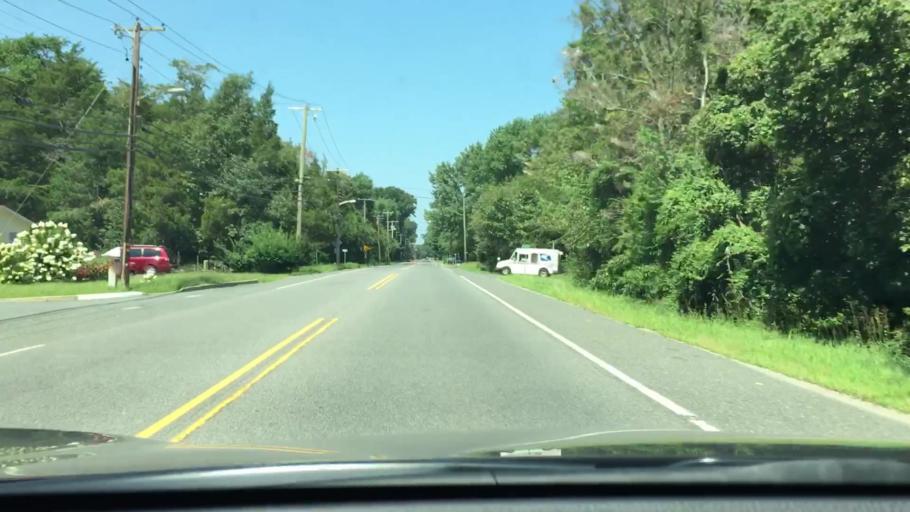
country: US
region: New Jersey
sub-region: Cumberland County
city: Laurel Lake
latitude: 39.3347
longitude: -75.0214
